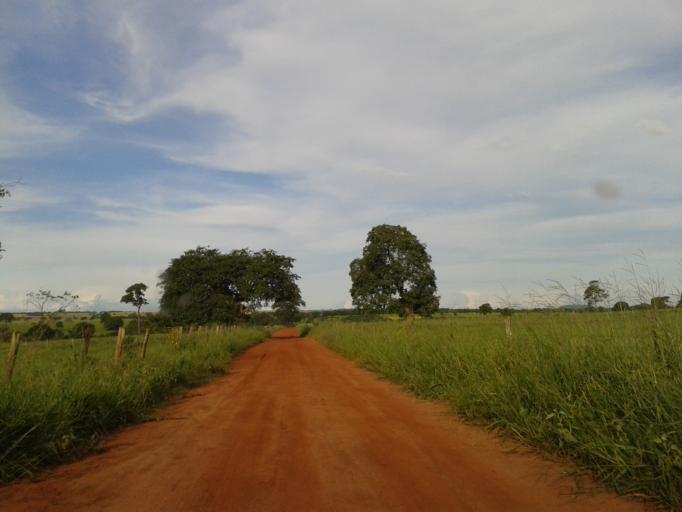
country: BR
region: Minas Gerais
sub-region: Capinopolis
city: Capinopolis
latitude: -18.7929
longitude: -49.8040
